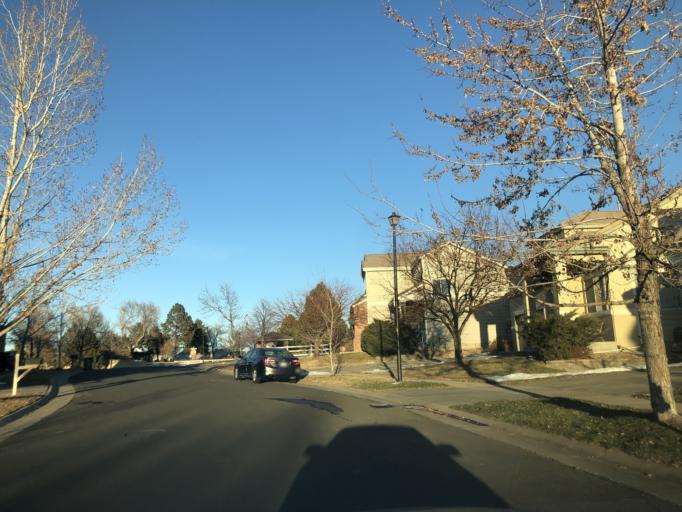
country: US
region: Colorado
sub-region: Adams County
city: Aurora
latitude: 39.7139
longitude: -104.8143
